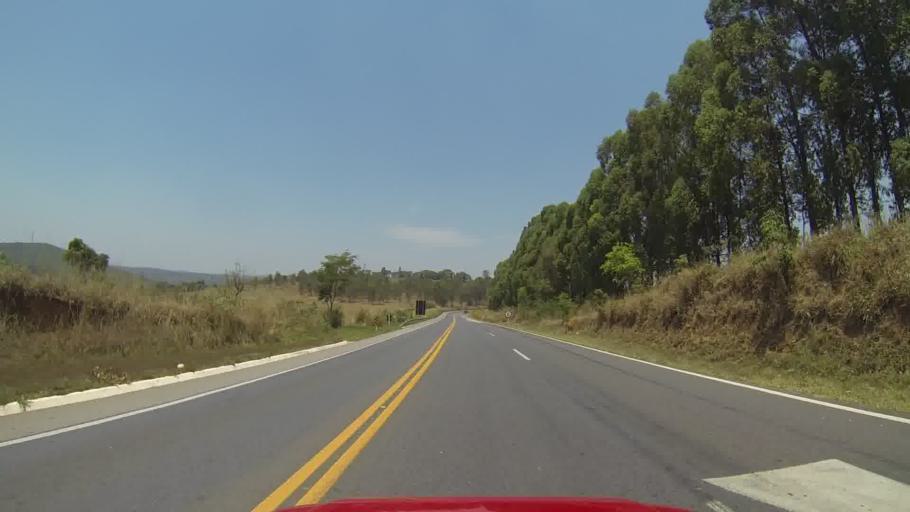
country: BR
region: Minas Gerais
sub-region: Itapecerica
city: Itapecerica
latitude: -20.3037
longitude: -45.2048
